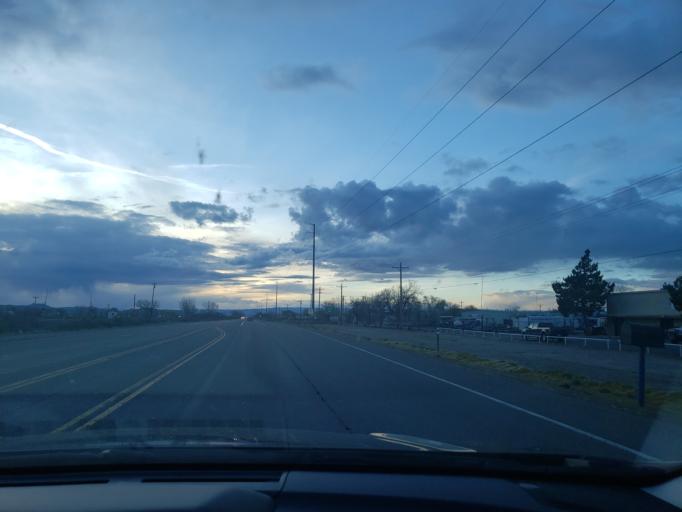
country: US
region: Colorado
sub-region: Mesa County
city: Fruita
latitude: 39.1286
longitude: -108.6808
